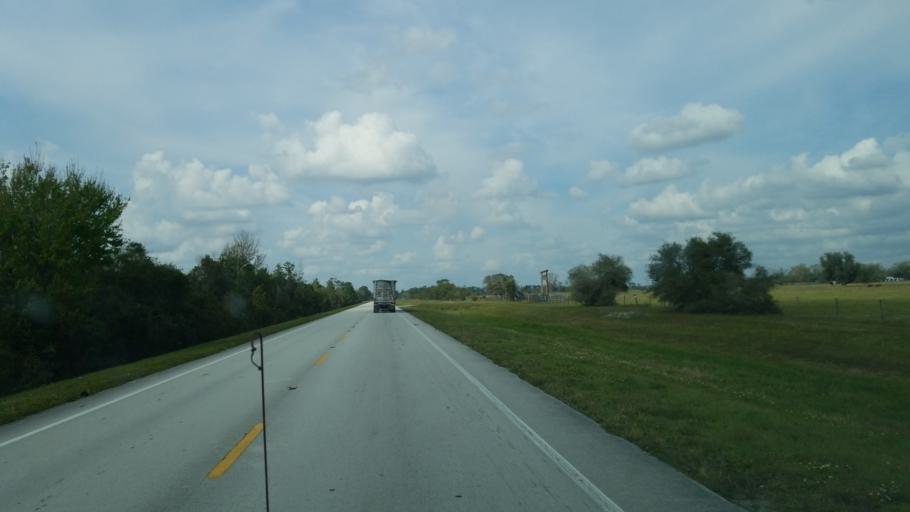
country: US
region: Florida
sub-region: Indian River County
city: Fellsmere
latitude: 27.7090
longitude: -80.9091
